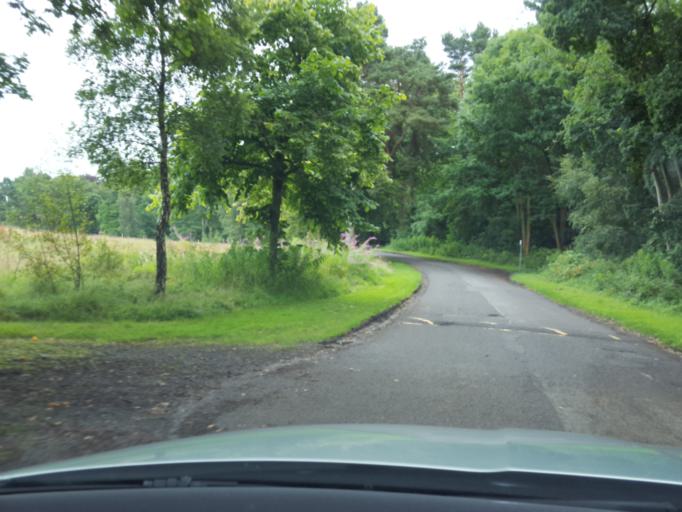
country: GB
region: Scotland
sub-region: Falkirk
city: Polmont
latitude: 55.9619
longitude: -3.6663
